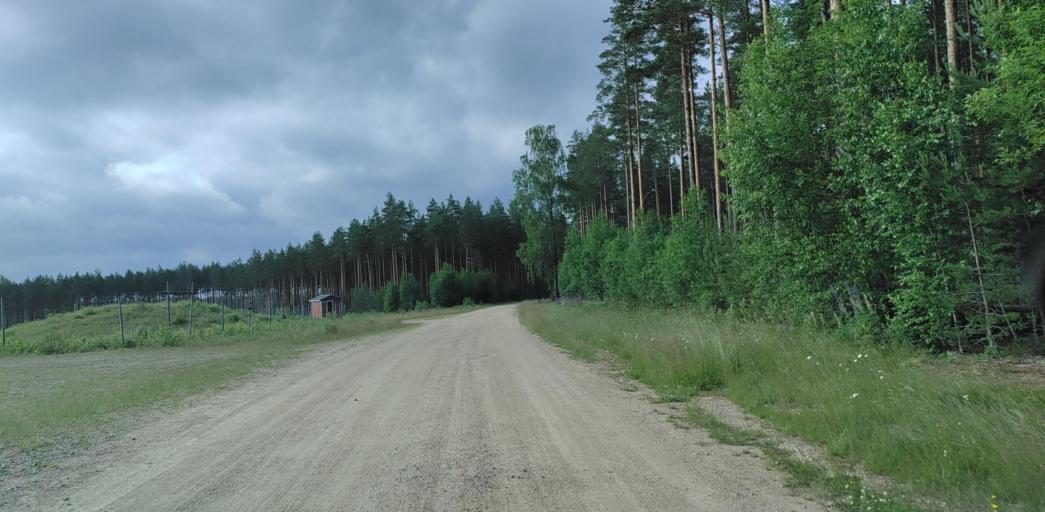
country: SE
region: Vaermland
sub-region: Hagfors Kommun
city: Hagfors
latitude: 60.0485
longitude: 13.5805
